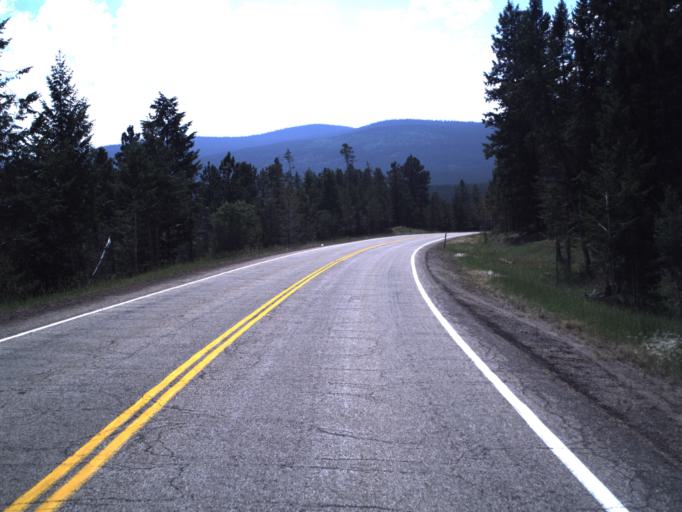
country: US
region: Utah
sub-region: Daggett County
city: Manila
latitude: 40.8470
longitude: -109.6669
